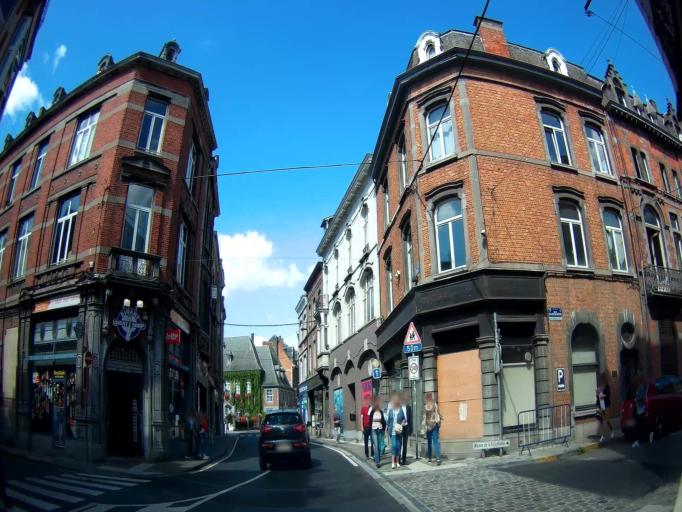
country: BE
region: Wallonia
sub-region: Province de Namur
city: Dinant
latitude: 50.2587
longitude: 4.9139
